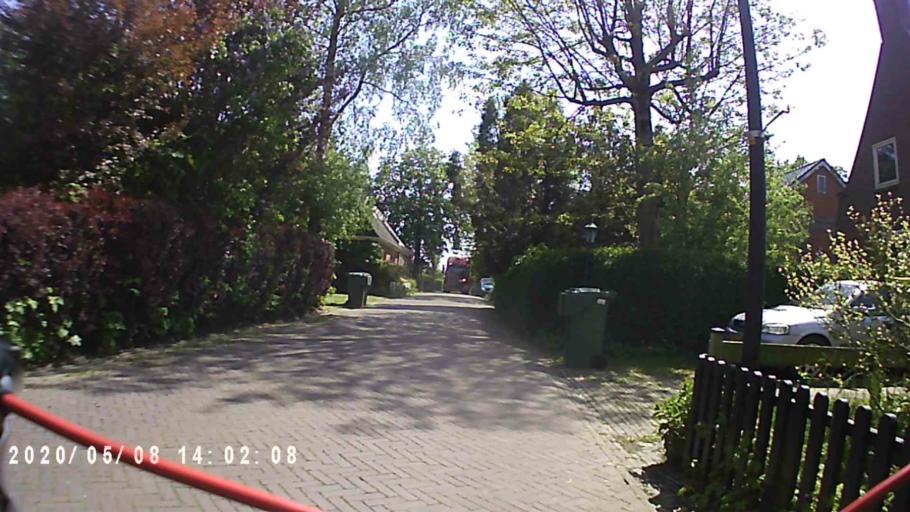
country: NL
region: Groningen
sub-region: Gemeente Appingedam
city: Appingedam
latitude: 53.3393
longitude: 6.8128
